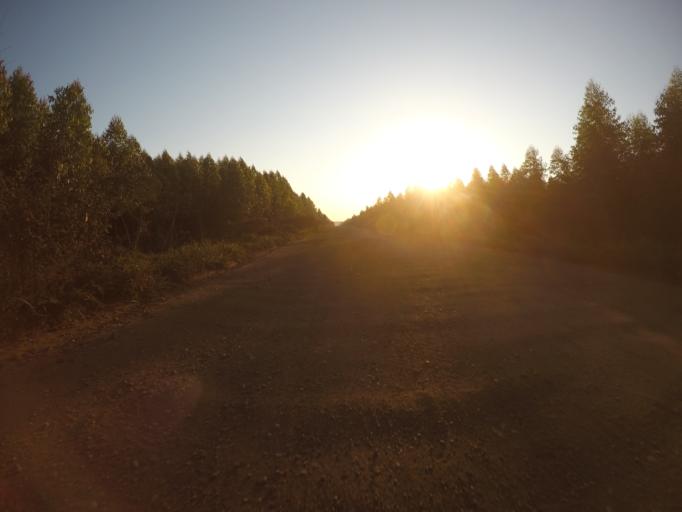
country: ZA
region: KwaZulu-Natal
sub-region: uThungulu District Municipality
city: KwaMbonambi
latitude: -28.6668
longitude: 32.0675
